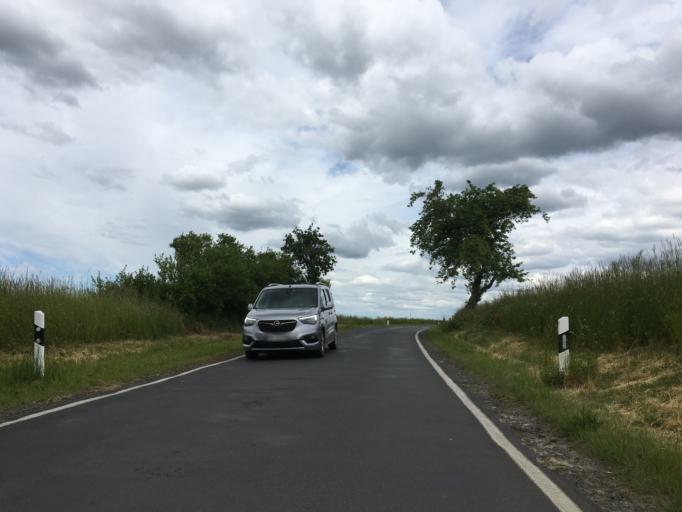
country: DE
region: Brandenburg
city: Hohenfinow
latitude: 52.7594
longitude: 13.8796
